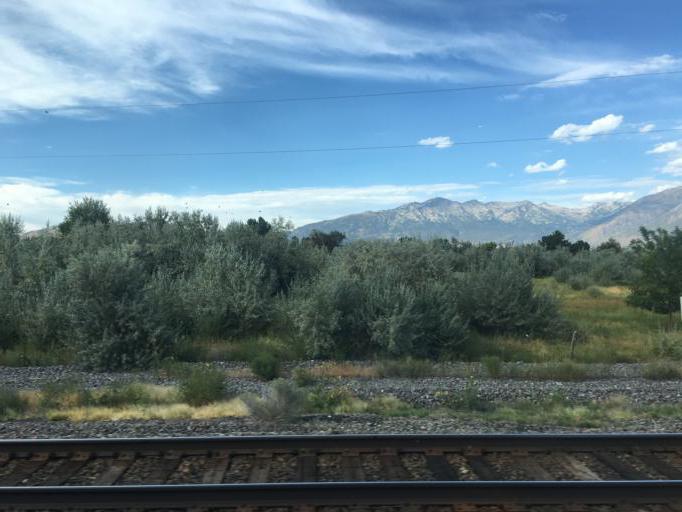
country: US
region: Utah
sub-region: Utah County
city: Lehi
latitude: 40.3797
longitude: -111.8441
